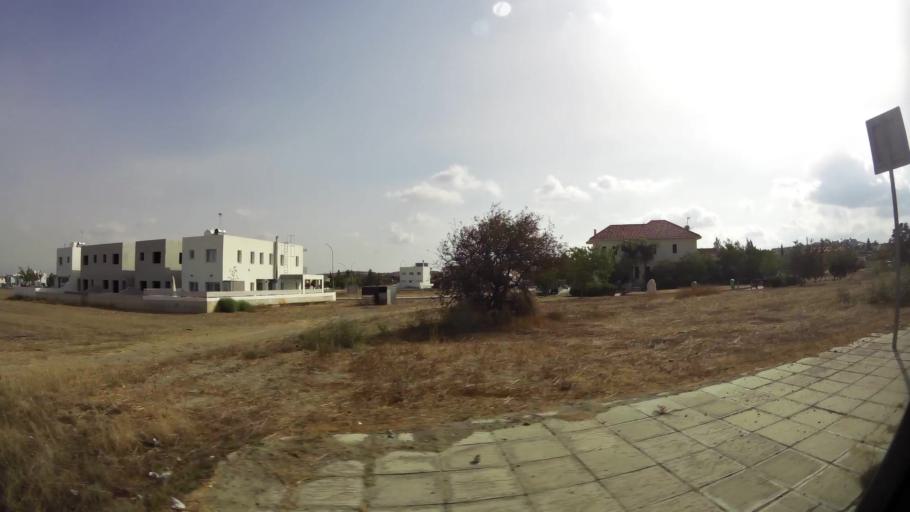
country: CY
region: Lefkosia
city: Geri
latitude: 35.0654
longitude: 33.3952
